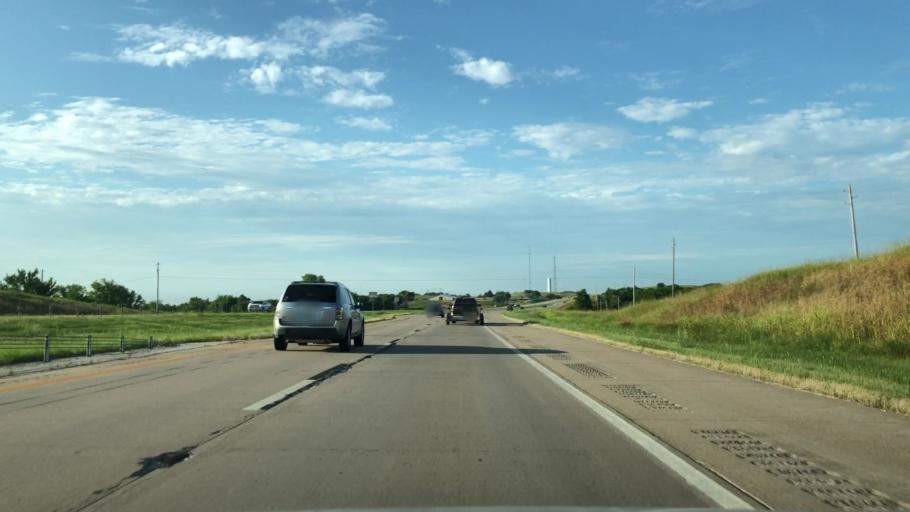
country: US
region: Oklahoma
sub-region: Osage County
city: Skiatook
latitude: 36.5120
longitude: -95.9217
